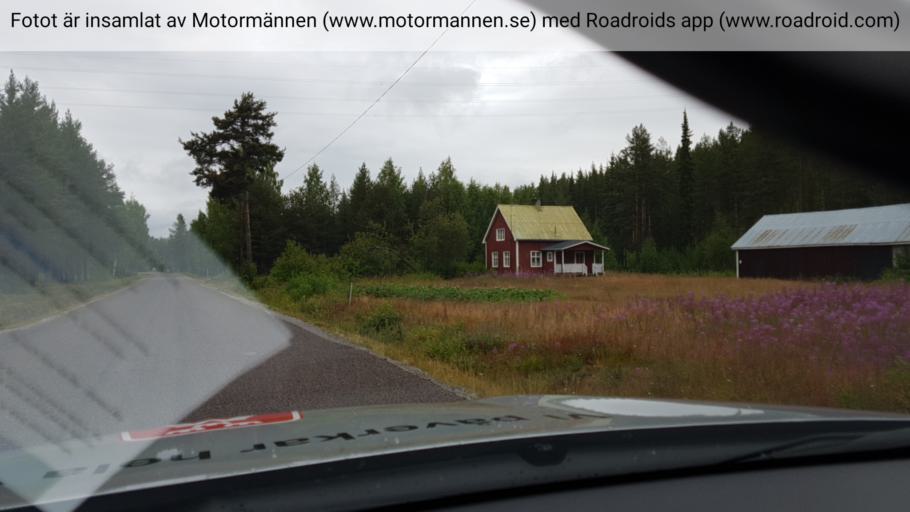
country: SE
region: Norrbotten
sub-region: Gallivare Kommun
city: Gaellivare
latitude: 66.4627
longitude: 20.6477
